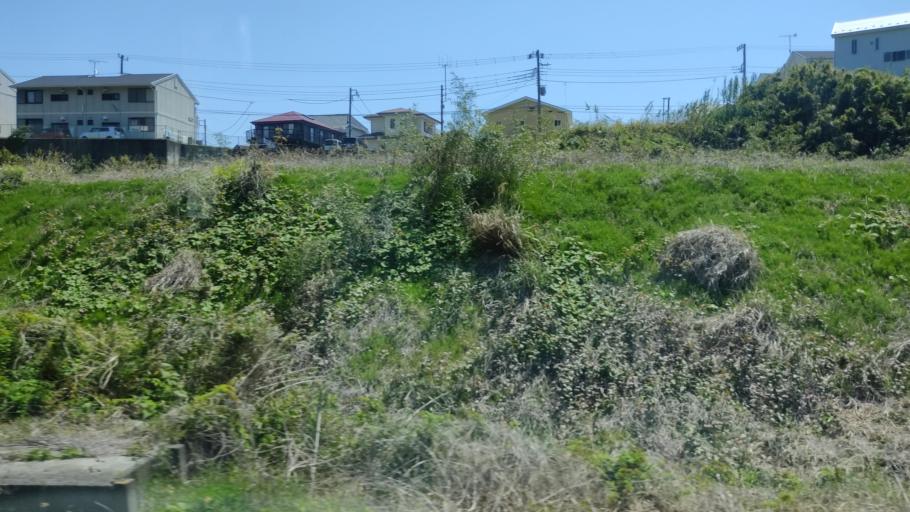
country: JP
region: Kanagawa
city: Ninomiya
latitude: 35.2875
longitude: 139.2284
